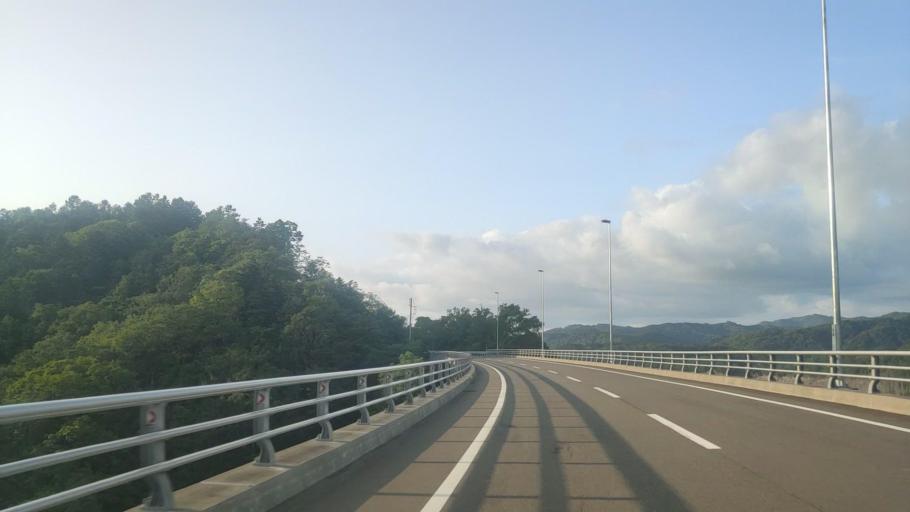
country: JP
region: Hokkaido
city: Bibai
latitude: 43.0699
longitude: 142.1044
